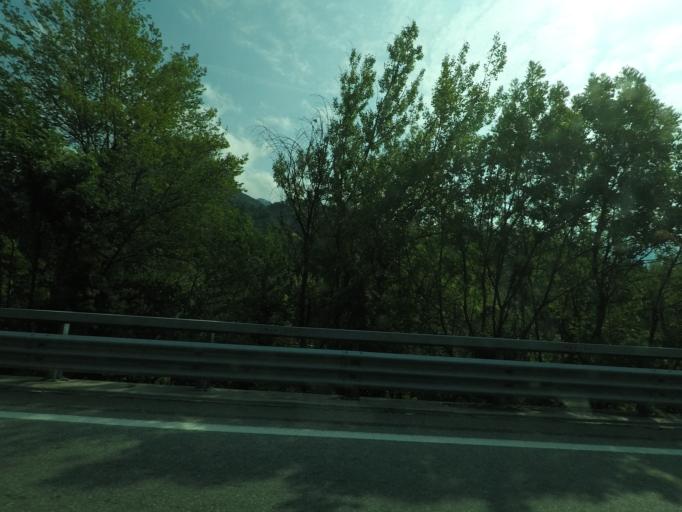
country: IT
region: Aosta Valley
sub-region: Valle d'Aosta
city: Chatillon
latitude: 45.7519
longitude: 7.6087
